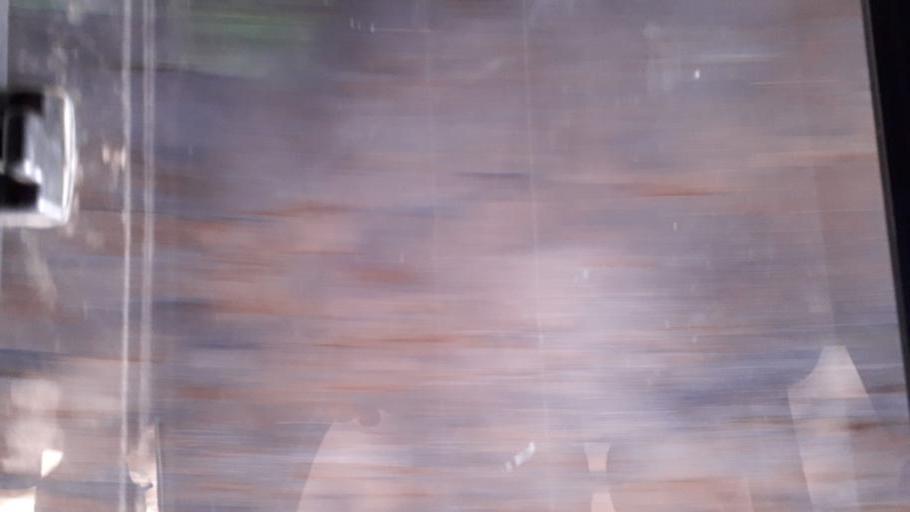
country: LS
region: Mokhotlong
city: Mokhotlong
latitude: -29.2782
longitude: 28.9328
